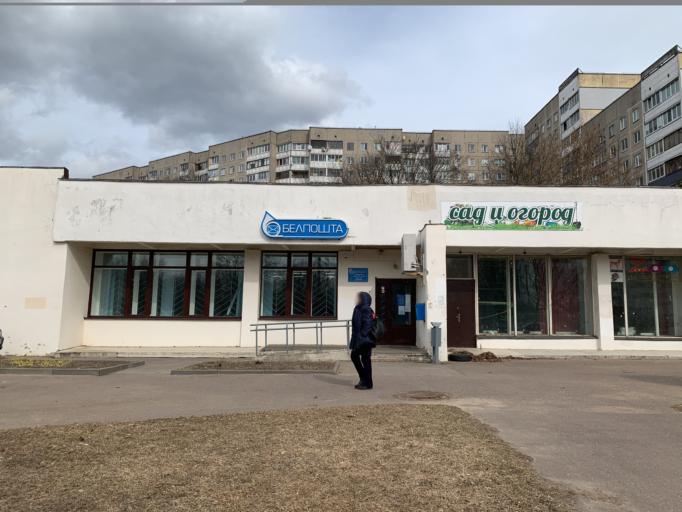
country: BY
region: Minsk
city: Borovlyany
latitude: 53.9524
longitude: 27.6334
